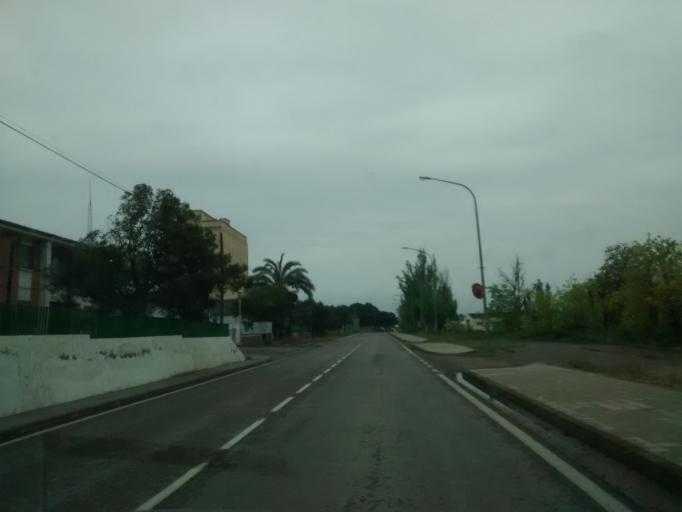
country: ES
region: Aragon
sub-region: Provincia de Zaragoza
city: Caspe
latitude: 41.2262
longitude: -0.0311
